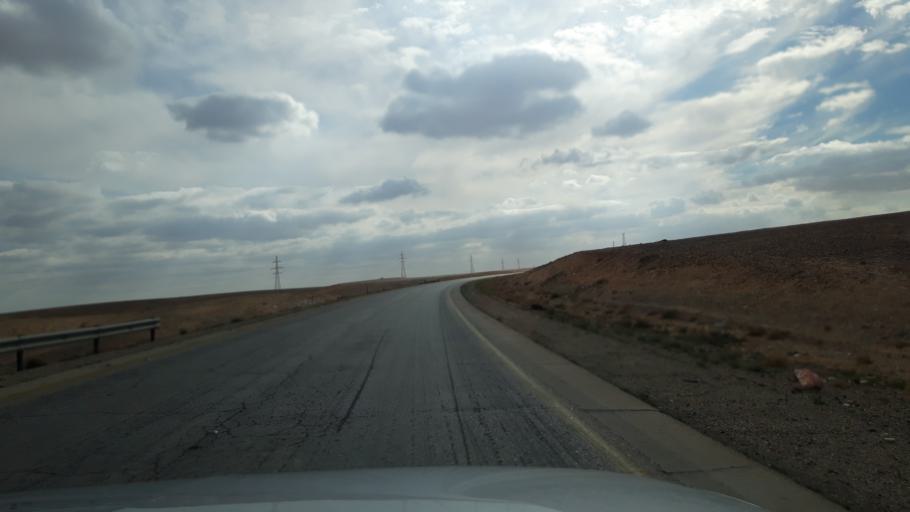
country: JO
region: Amman
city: Al Azraq ash Shamali
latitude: 31.7437
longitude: 36.5350
